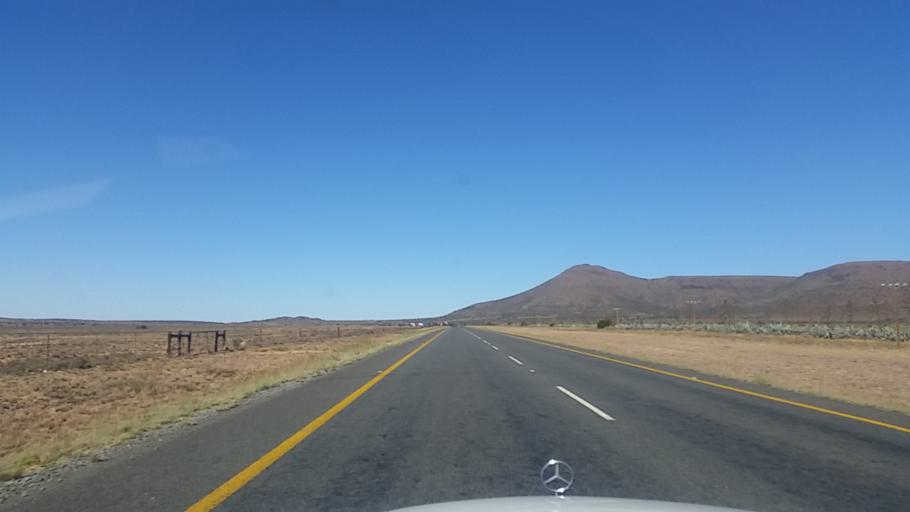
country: ZA
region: Eastern Cape
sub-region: Cacadu District Municipality
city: Graaff-Reinet
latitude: -32.0252
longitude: 24.6330
